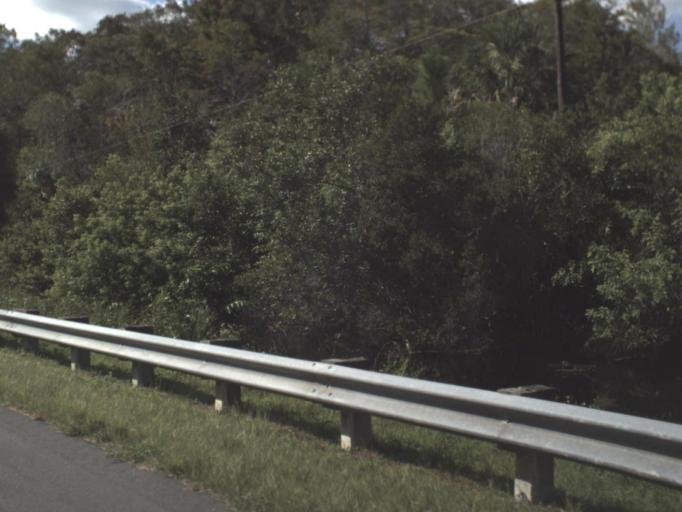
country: US
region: Florida
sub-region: Collier County
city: Marco
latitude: 25.8762
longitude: -81.2234
